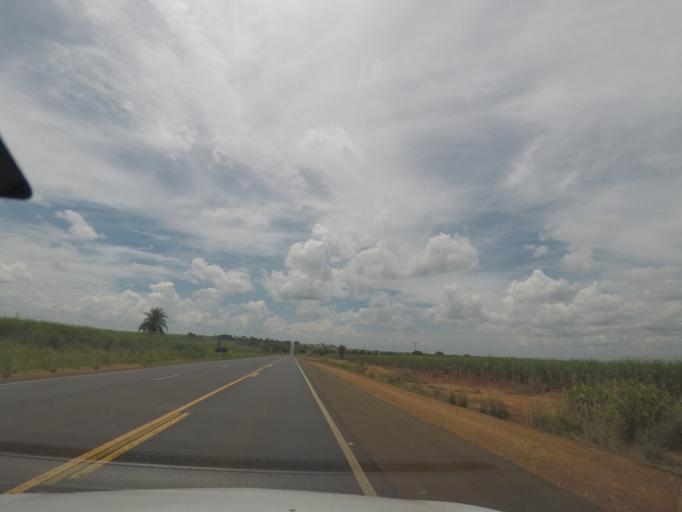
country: BR
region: Sao Paulo
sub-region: Barretos
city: Barretos
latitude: -20.4118
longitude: -48.6333
